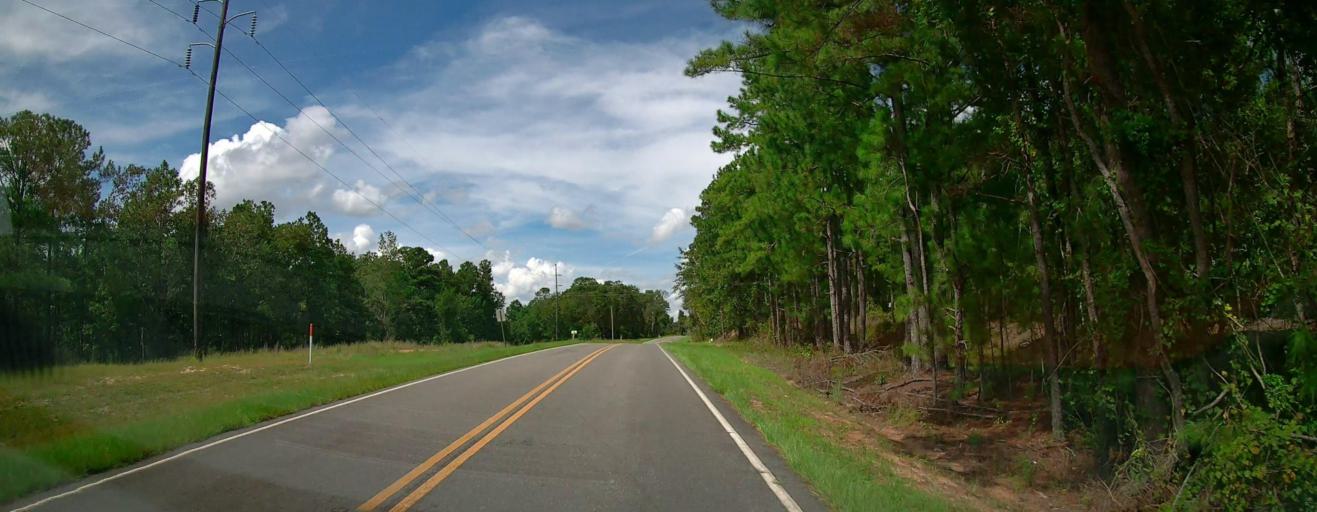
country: US
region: Georgia
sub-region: Taylor County
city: Butler
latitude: 32.5131
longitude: -84.2045
